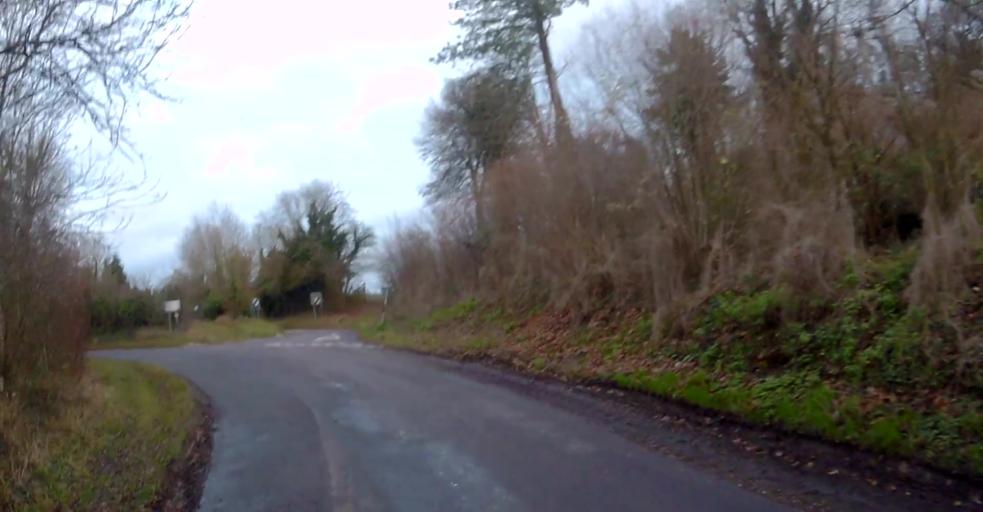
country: GB
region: England
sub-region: Hampshire
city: Overton
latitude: 51.2523
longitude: -1.2559
